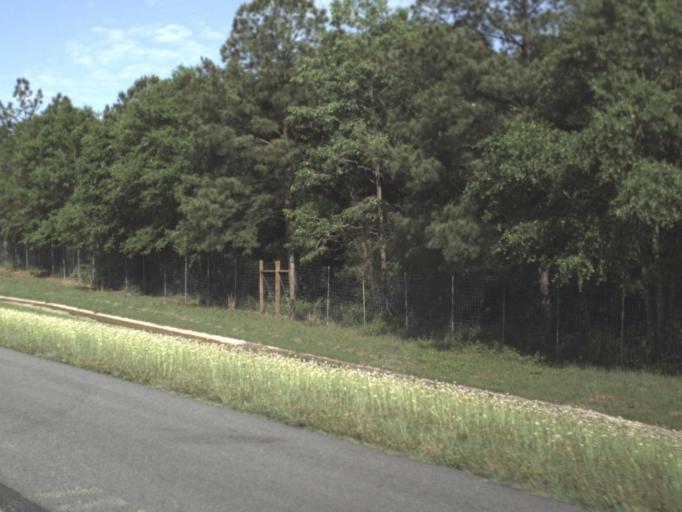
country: US
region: Florida
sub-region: Walton County
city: DeFuniak Springs
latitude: 30.7232
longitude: -85.9134
